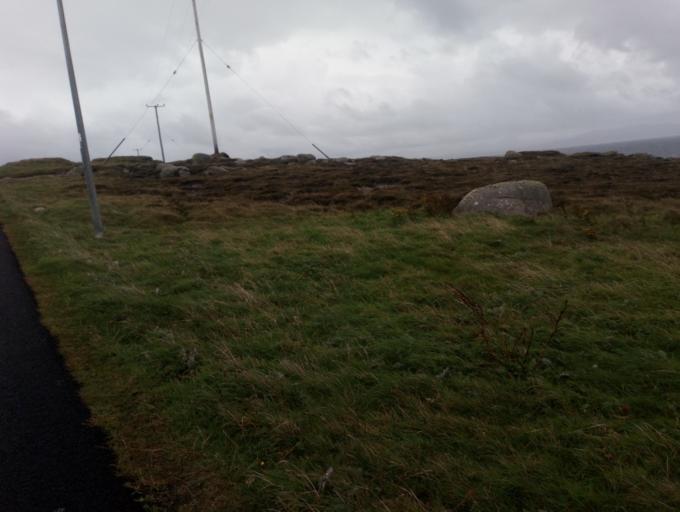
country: IE
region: Ulster
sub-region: County Donegal
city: Derrybeg
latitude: 55.2635
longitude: -8.2206
